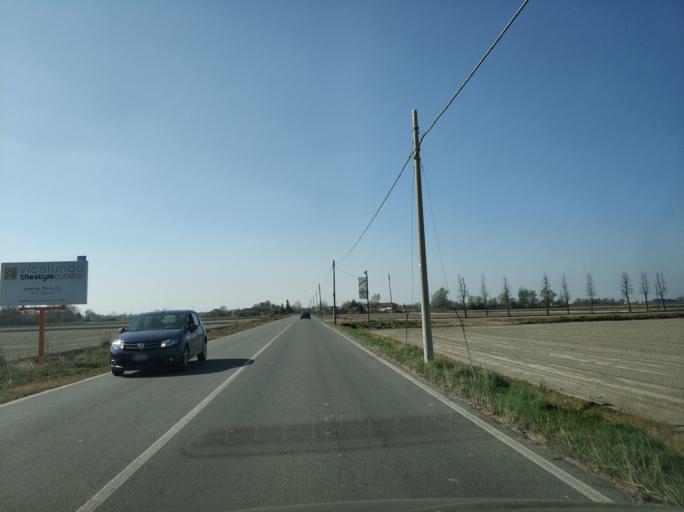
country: IT
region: Piedmont
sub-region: Provincia di Vercelli
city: Borgo Vercelli
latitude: 45.3265
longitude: 8.4677
